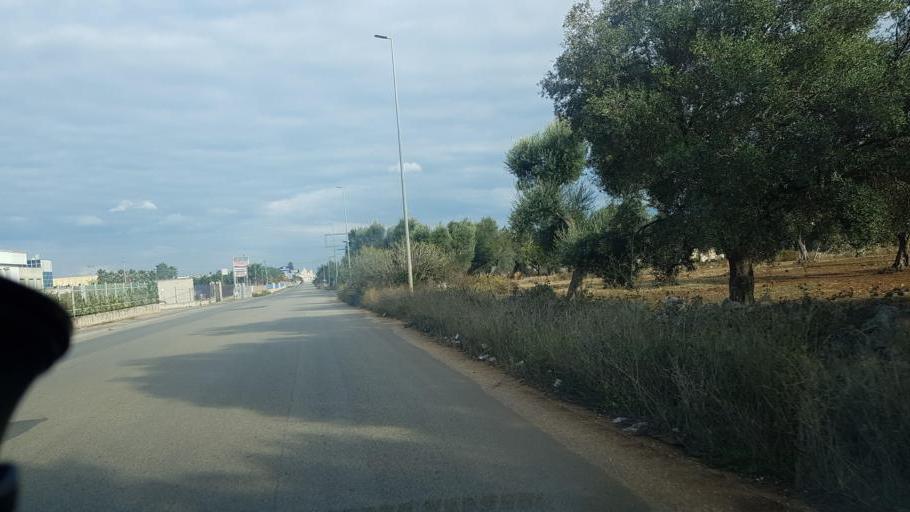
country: IT
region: Apulia
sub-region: Provincia di Brindisi
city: Francavilla Fontana
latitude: 40.5326
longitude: 17.5471
